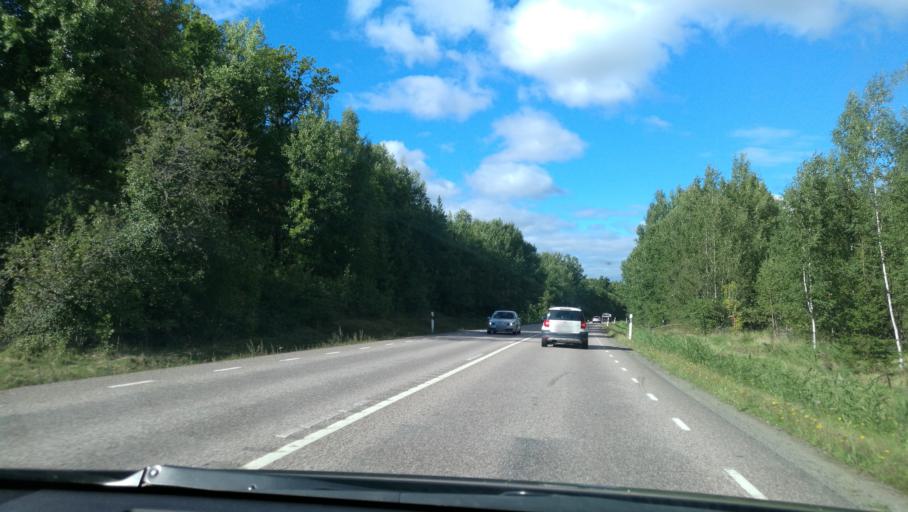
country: SE
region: Soedermanland
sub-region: Eskilstuna Kommun
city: Kvicksund
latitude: 59.4747
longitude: 16.3062
